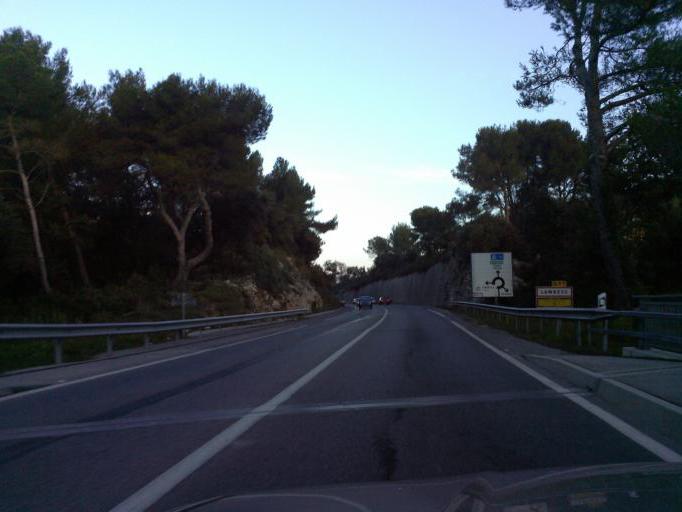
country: FR
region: Provence-Alpes-Cote d'Azur
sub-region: Departement des Bouches-du-Rhone
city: Lambesc
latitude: 43.6517
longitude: 5.2726
